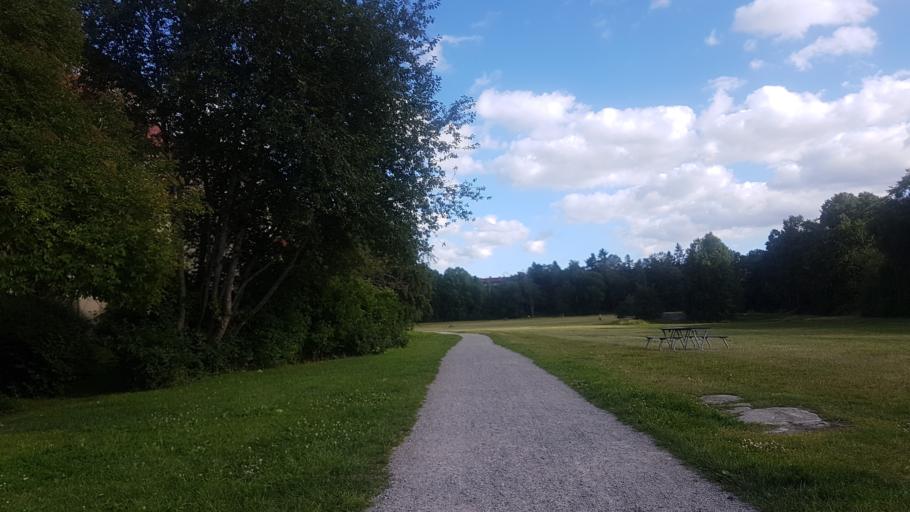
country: SE
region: Stockholm
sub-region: Stockholms Kommun
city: OEstermalm
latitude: 59.2904
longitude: 18.1099
